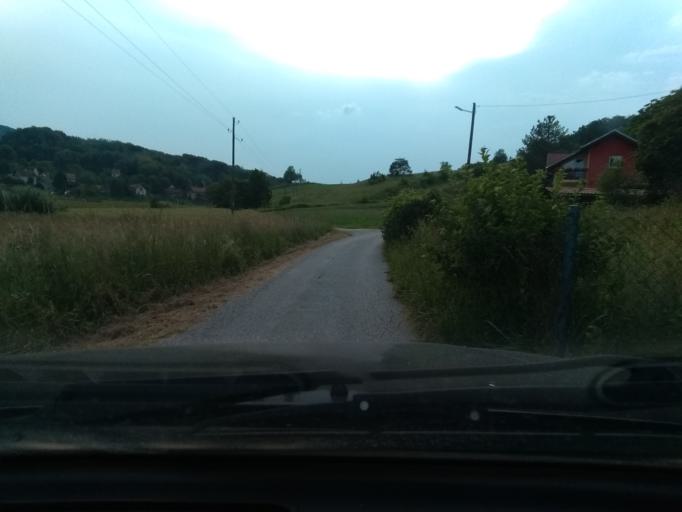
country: SI
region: Bistrica ob Sotli
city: Bistrica ob Sotli
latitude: 46.0760
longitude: 15.7464
